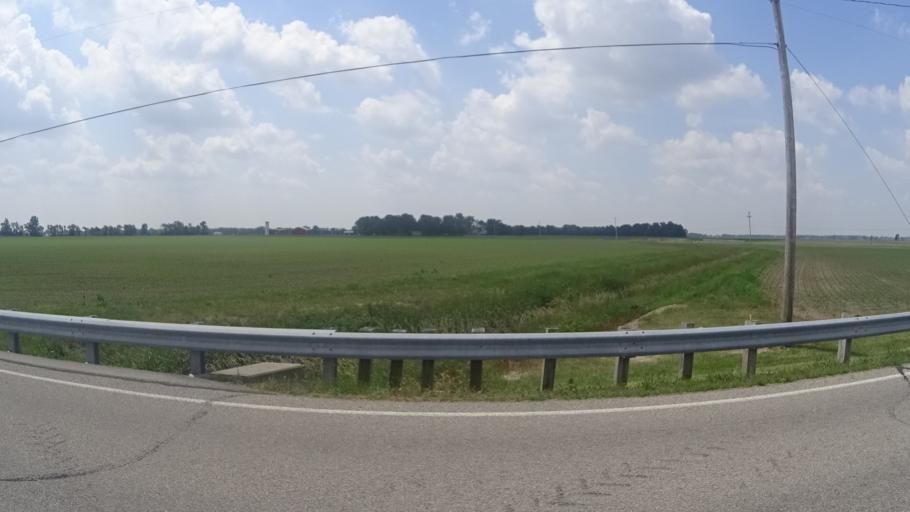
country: US
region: Ohio
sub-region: Huron County
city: Monroeville
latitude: 41.3238
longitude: -82.7162
